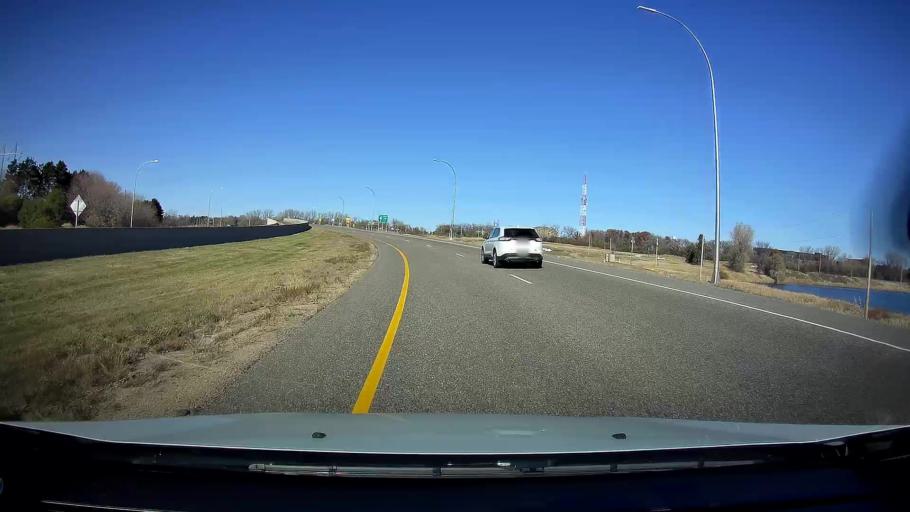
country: US
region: Minnesota
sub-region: Ramsey County
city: Arden Hills
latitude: 45.0584
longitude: -93.1570
